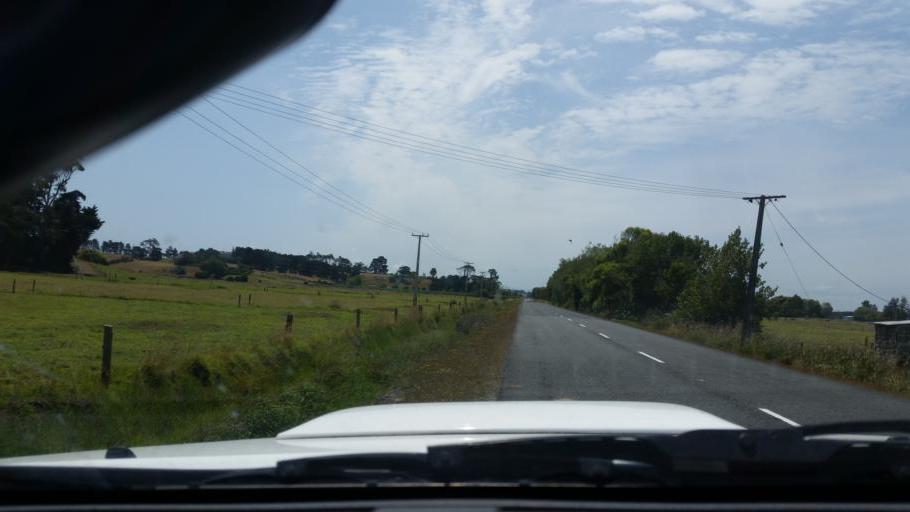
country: NZ
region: Northland
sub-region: Kaipara District
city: Dargaville
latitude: -36.0667
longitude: 173.9400
